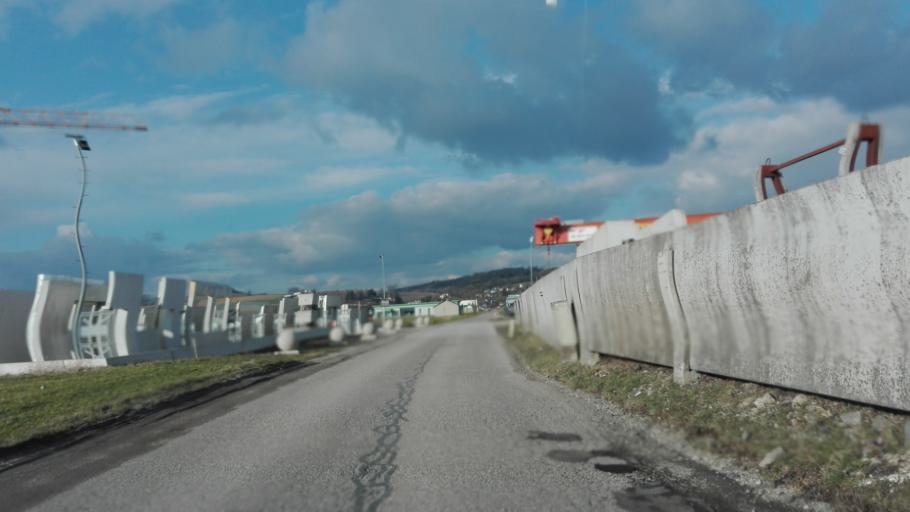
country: AT
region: Upper Austria
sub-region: Politischer Bezirk Perg
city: Perg
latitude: 48.2399
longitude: 14.6205
